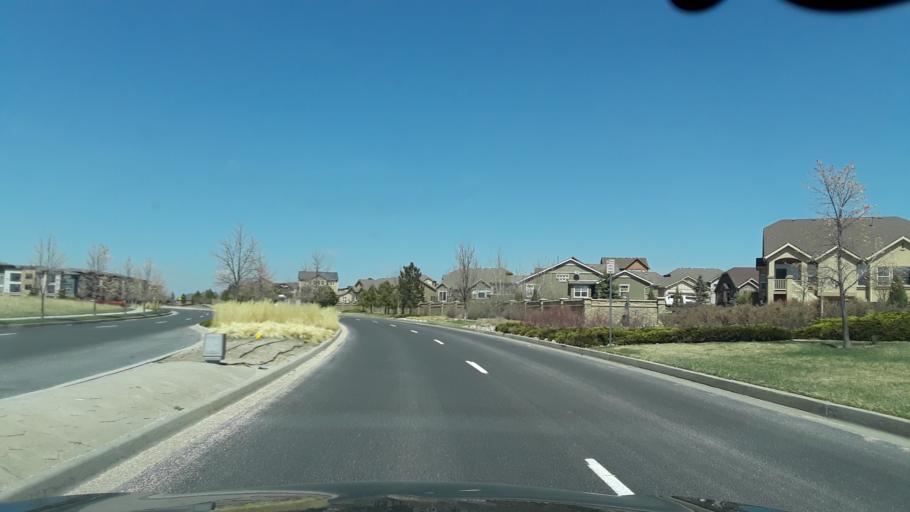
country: US
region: Colorado
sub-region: El Paso County
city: Black Forest
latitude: 38.9720
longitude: -104.7386
